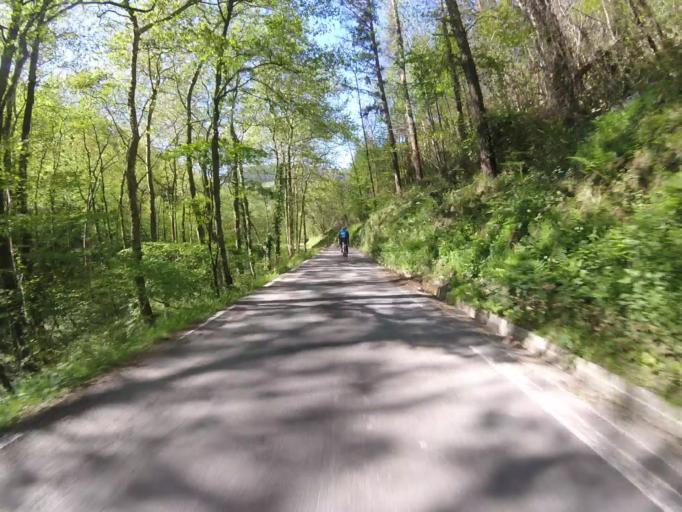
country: ES
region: Basque Country
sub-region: Provincia de Guipuzcoa
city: Errezil
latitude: 43.1800
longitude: -2.2034
